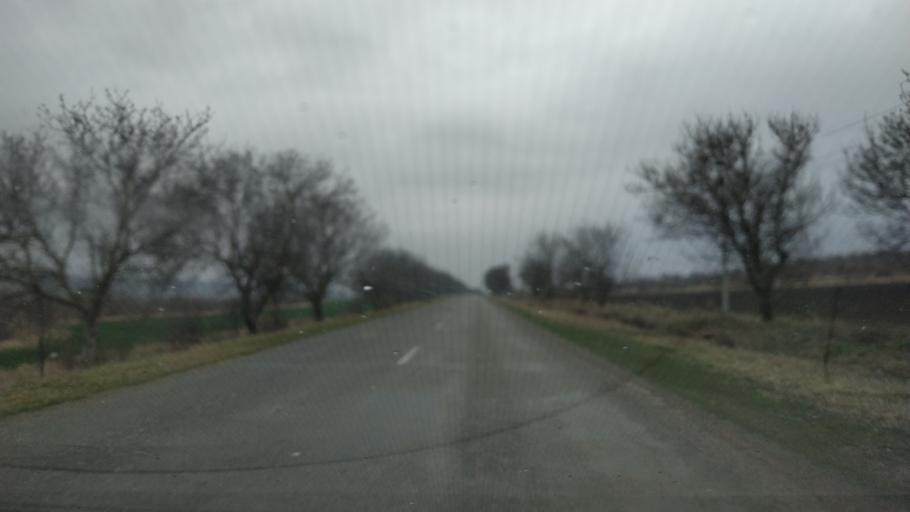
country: MD
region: Cantemir
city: Cantemir
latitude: 46.3064
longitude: 28.2604
